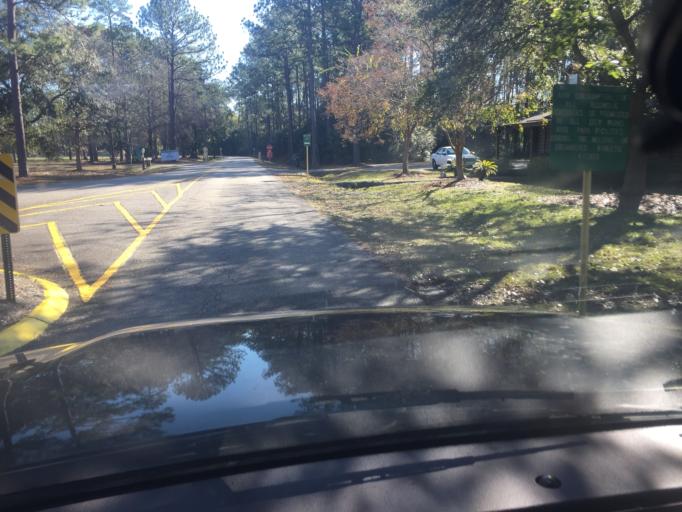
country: US
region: Louisiana
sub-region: Saint Tammany Parish
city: Slidell
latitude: 30.3056
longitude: -89.7497
